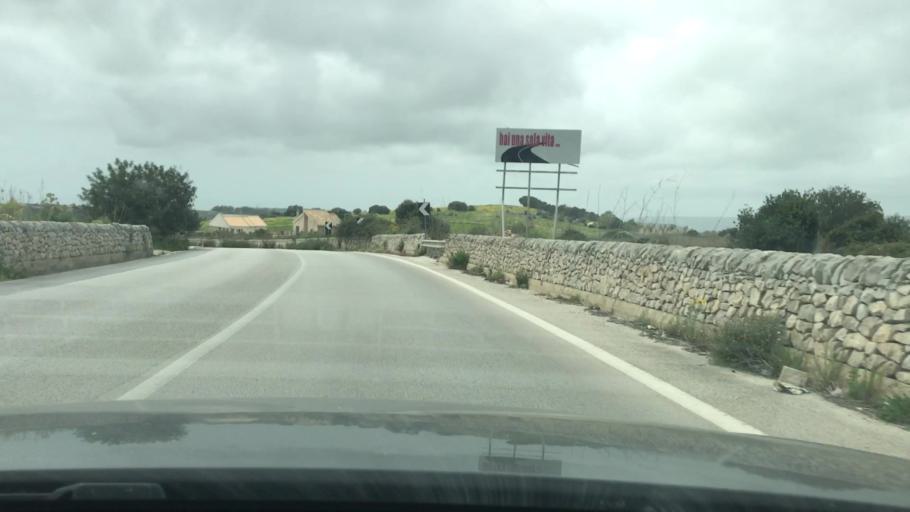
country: IT
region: Sicily
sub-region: Ragusa
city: Scicli
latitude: 36.8163
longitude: 14.7359
